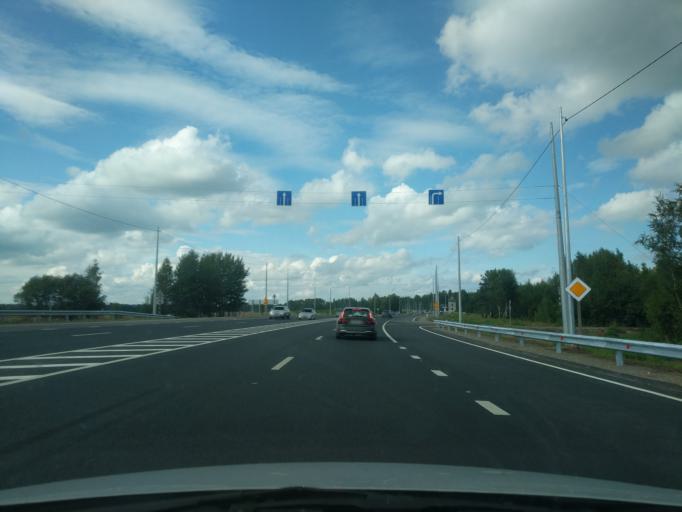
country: RU
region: Kostroma
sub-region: Kostromskoy Rayon
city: Kostroma
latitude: 57.7327
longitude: 40.8689
